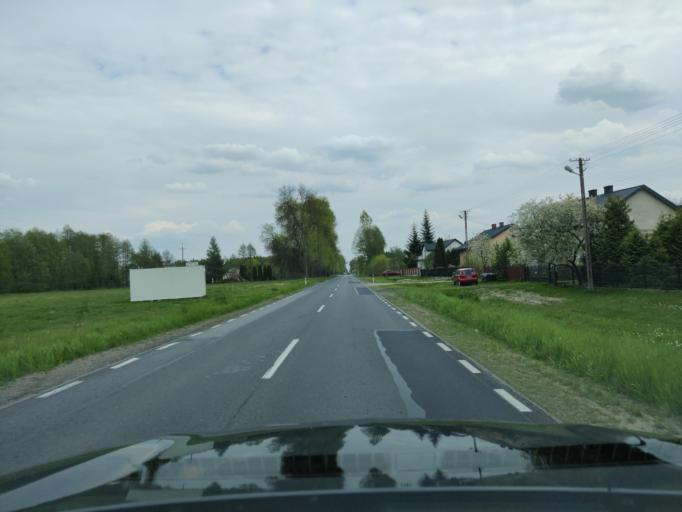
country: PL
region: Masovian Voivodeship
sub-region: Powiat wyszkowski
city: Rzasnik
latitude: 52.6205
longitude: 21.3558
